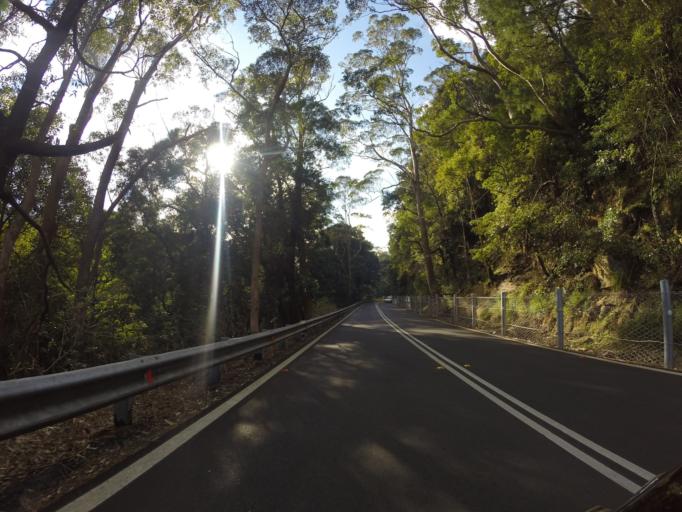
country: AU
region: New South Wales
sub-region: Wollongong
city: Mount Keira
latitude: -34.4028
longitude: 150.8493
